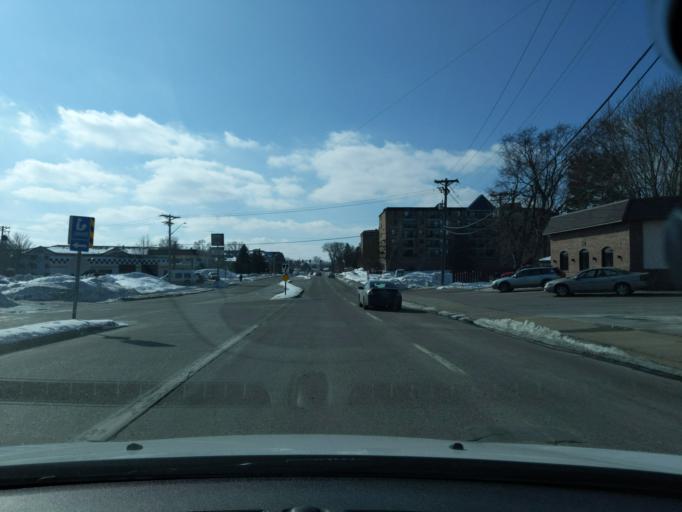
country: US
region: Minnesota
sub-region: Hennepin County
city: Saint Anthony
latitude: 45.0166
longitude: -93.2200
